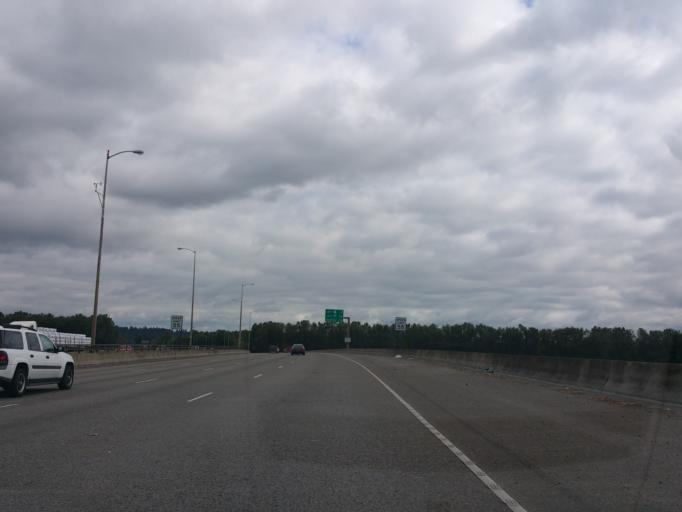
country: US
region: Washington
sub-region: Clark County
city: Mill Plain
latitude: 45.5748
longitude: -122.5459
